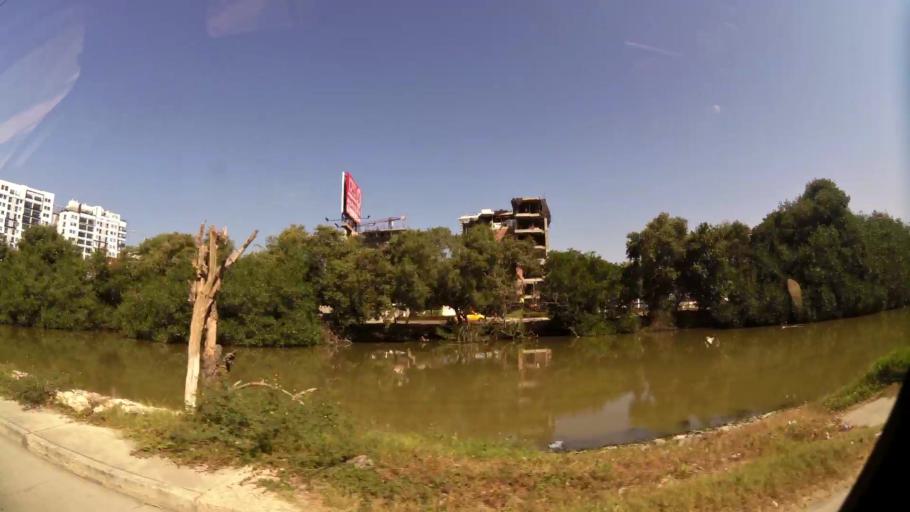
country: CO
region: Bolivar
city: Cartagena
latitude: 10.4425
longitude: -75.5192
